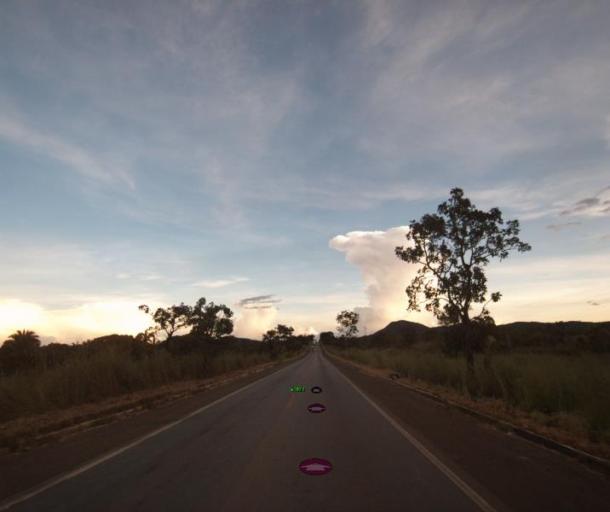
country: BR
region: Goias
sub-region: Uruacu
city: Uruacu
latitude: -14.3587
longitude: -49.1585
